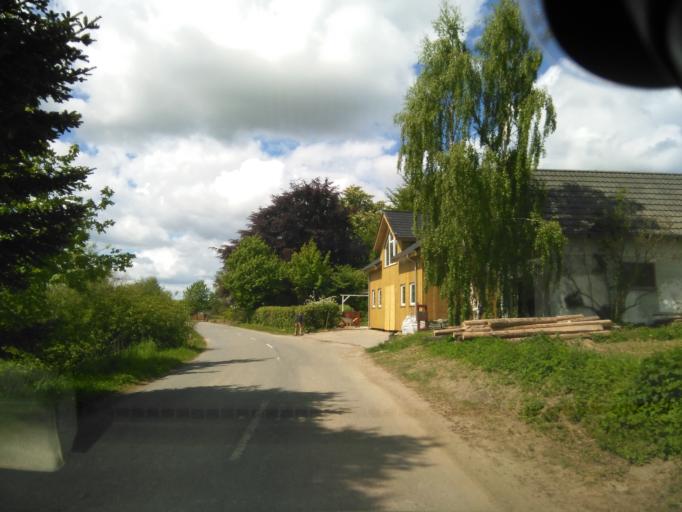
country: DK
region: Central Jutland
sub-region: Arhus Kommune
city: Solbjerg
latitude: 56.0259
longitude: 10.1130
